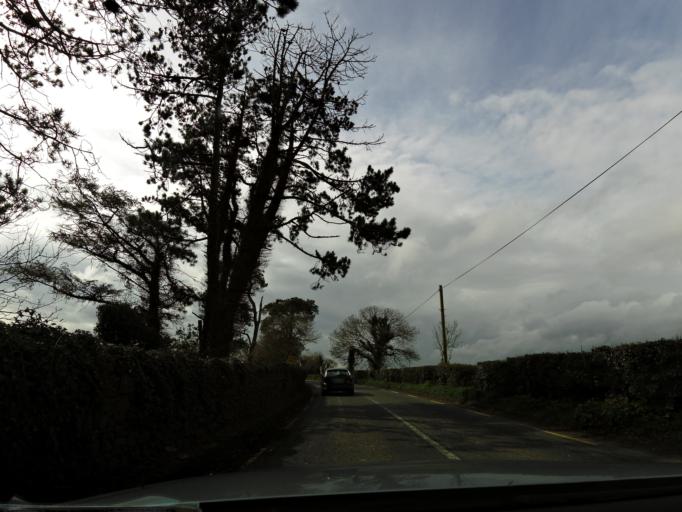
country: IE
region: Leinster
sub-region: Laois
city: Rathdowney
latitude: 52.7223
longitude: -7.5600
